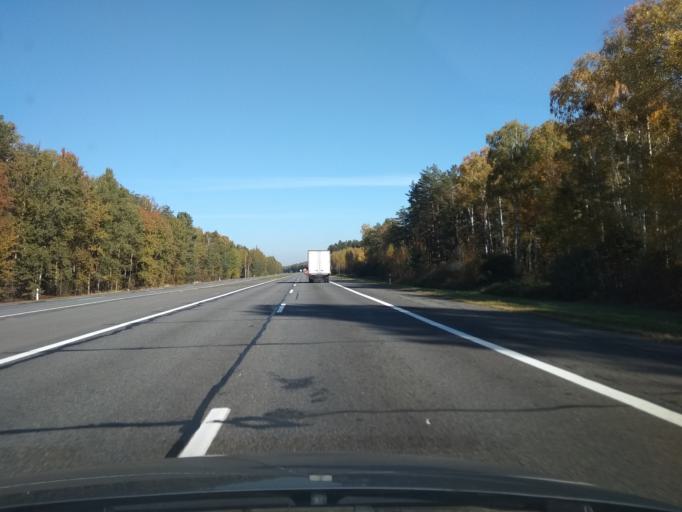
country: BY
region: Brest
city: Ivatsevichy
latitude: 52.7638
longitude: 25.5257
